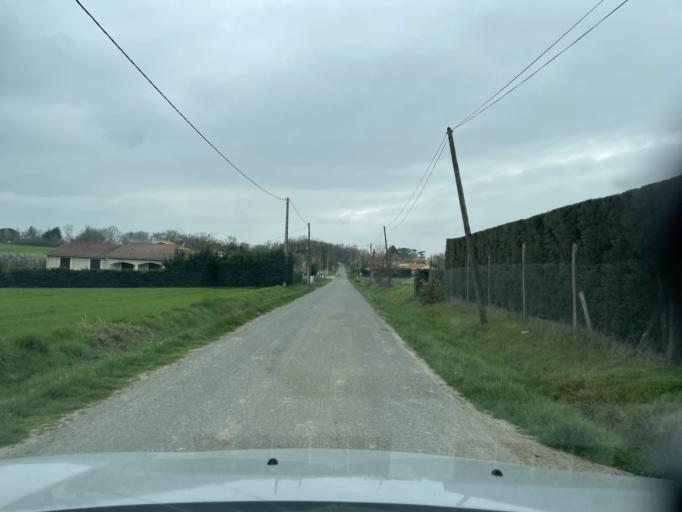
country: FR
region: Midi-Pyrenees
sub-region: Departement du Gers
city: Pujaudran
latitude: 43.6112
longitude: 1.1651
